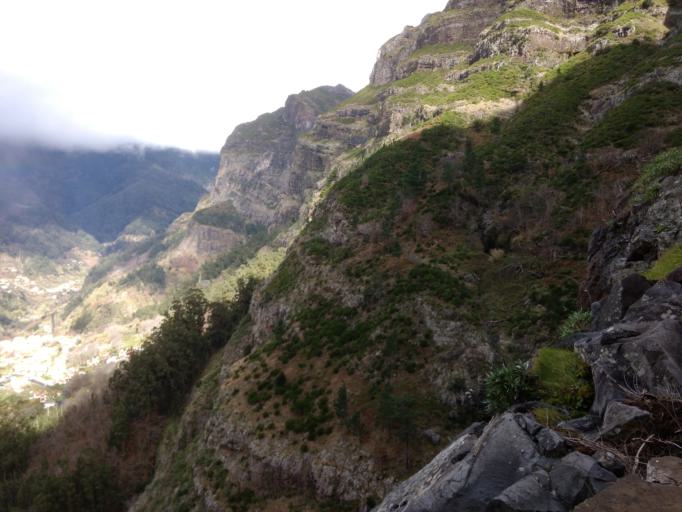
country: PT
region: Madeira
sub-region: Camara de Lobos
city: Curral das Freiras
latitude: 32.7162
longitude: -16.9612
